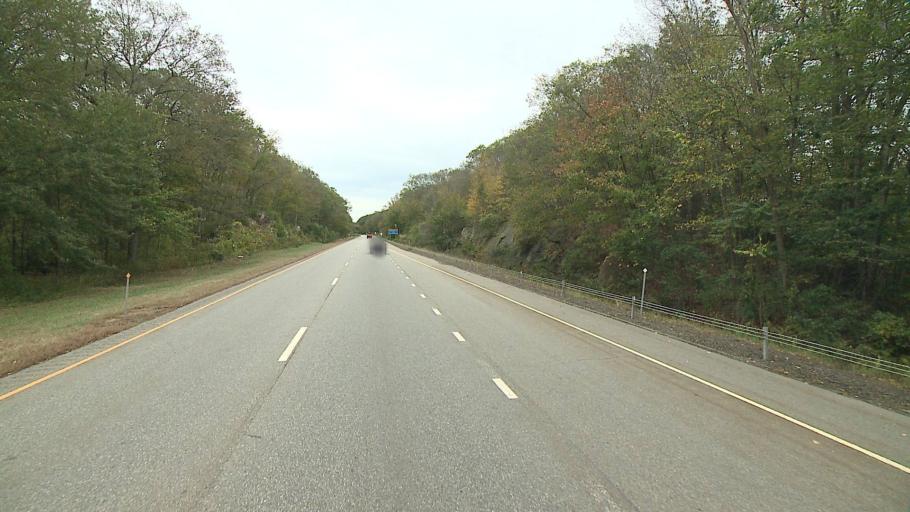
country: US
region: Connecticut
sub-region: Middlesex County
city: Deep River Center
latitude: 41.3600
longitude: -72.4218
